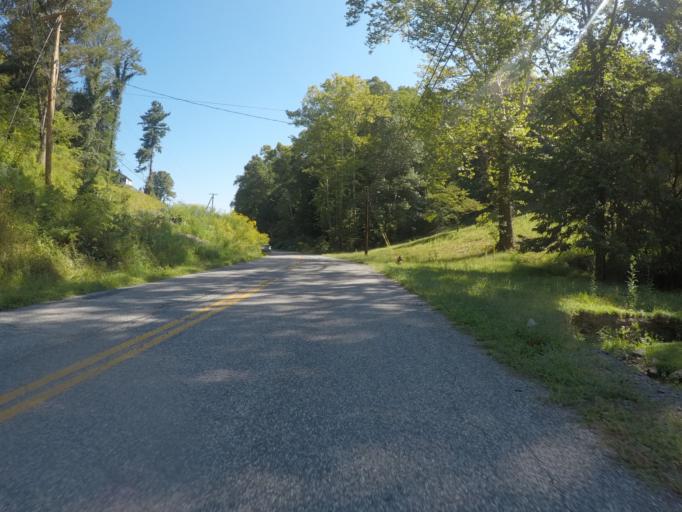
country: US
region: Kentucky
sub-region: Greenup County
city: Russell
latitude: 38.5244
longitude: -82.6920
